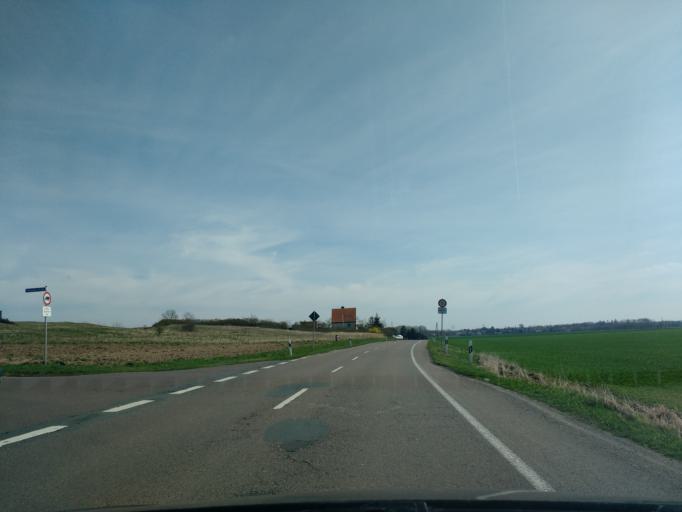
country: DE
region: Saxony-Anhalt
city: Halle (Saale)
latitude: 51.4903
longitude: 12.0201
